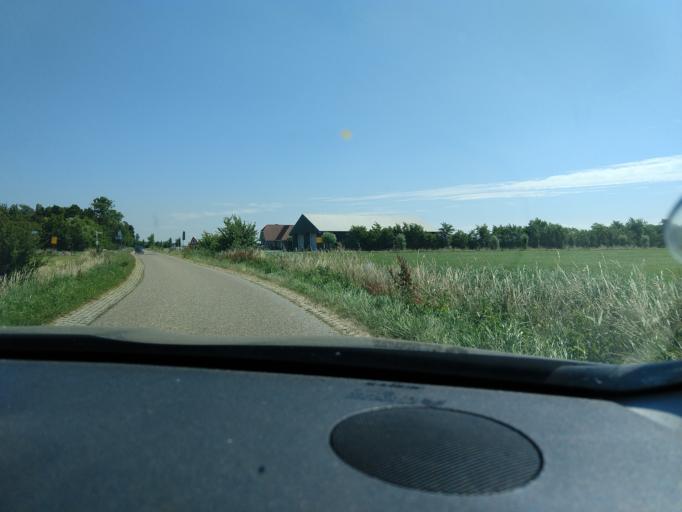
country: NL
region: Zeeland
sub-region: Gemeente Veere
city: Veere
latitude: 51.5257
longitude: 3.6675
